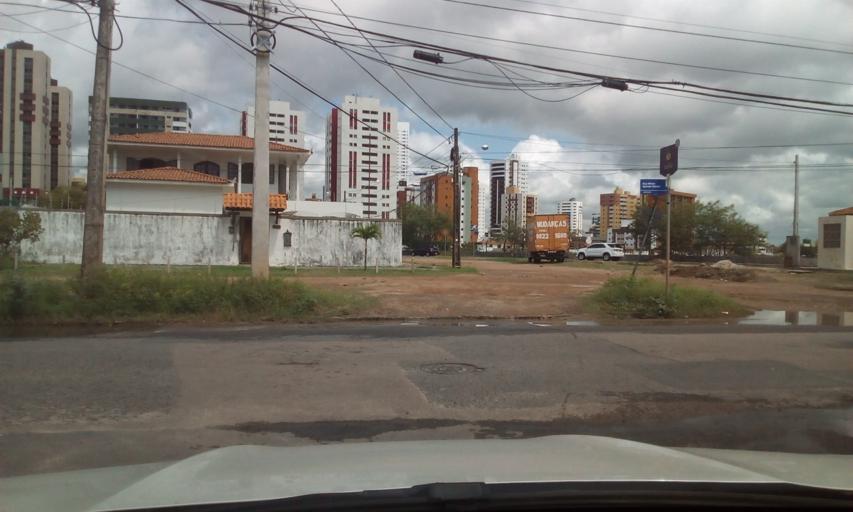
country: BR
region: Paraiba
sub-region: Joao Pessoa
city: Joao Pessoa
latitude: -7.0958
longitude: -34.8382
